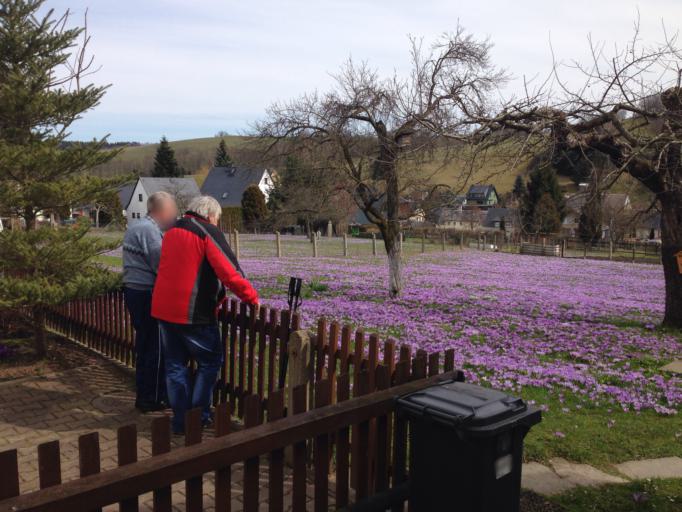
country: DE
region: Saxony
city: Venusberg
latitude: 50.6826
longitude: 13.0199
